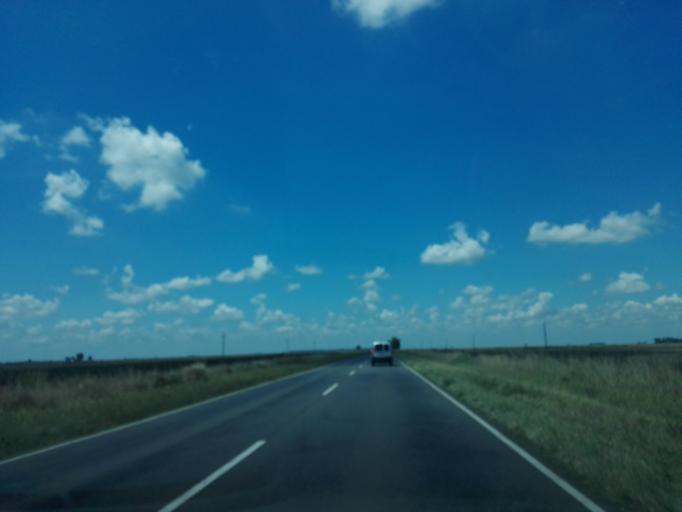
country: AR
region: Buenos Aires
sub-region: Partido de General Belgrano
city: General Belgrano
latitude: -35.9418
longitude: -58.6203
